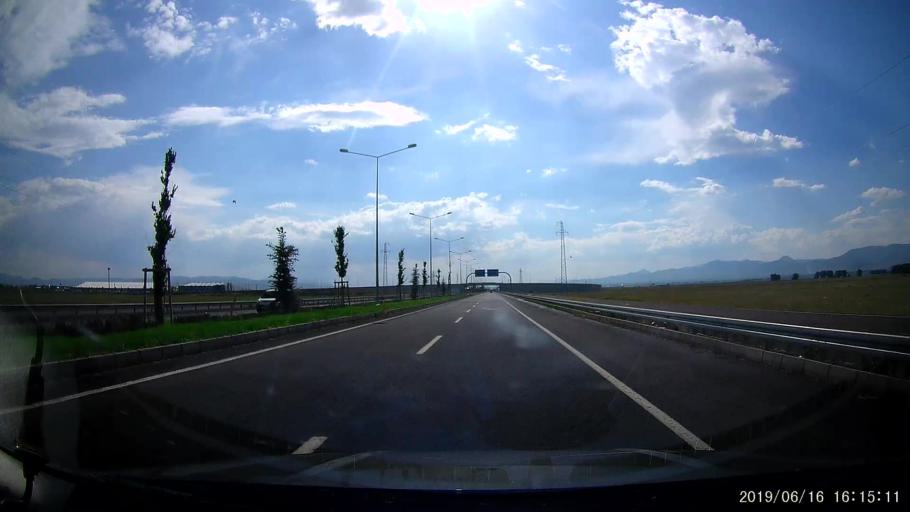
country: TR
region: Erzurum
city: Erzurum
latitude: 39.9616
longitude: 41.2317
